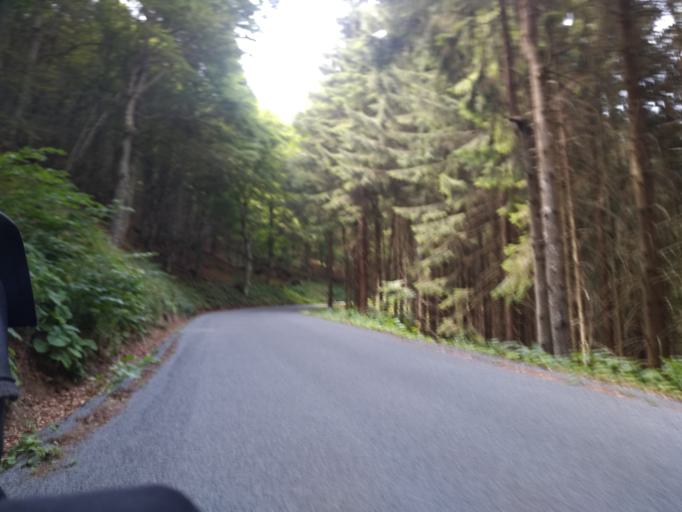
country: FR
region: Auvergne
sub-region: Departement du Cantal
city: Riom-es-Montagnes
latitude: 45.1332
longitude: 2.7030
